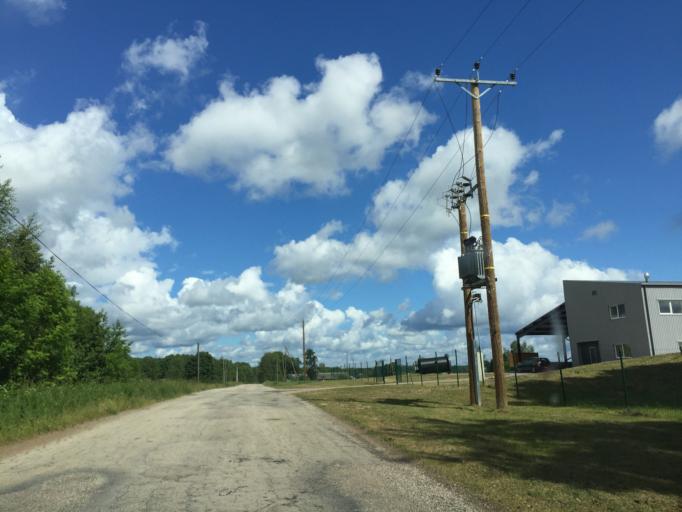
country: LV
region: Lecava
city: Iecava
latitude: 56.6082
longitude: 24.1916
